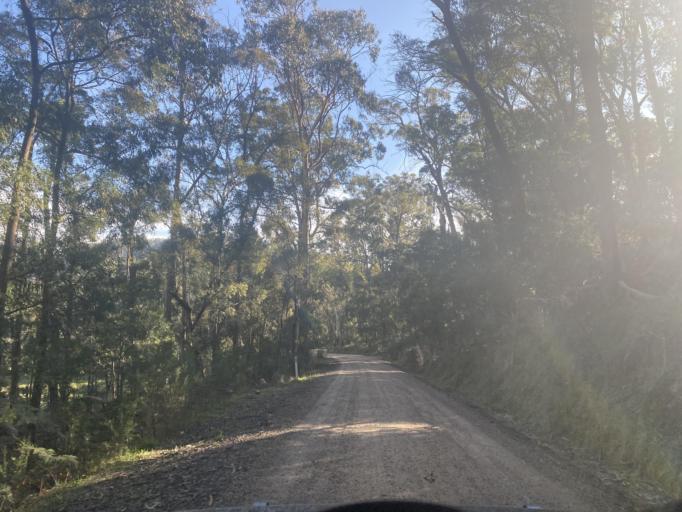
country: AU
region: Victoria
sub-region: Mansfield
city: Mansfield
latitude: -36.8263
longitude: 146.1451
